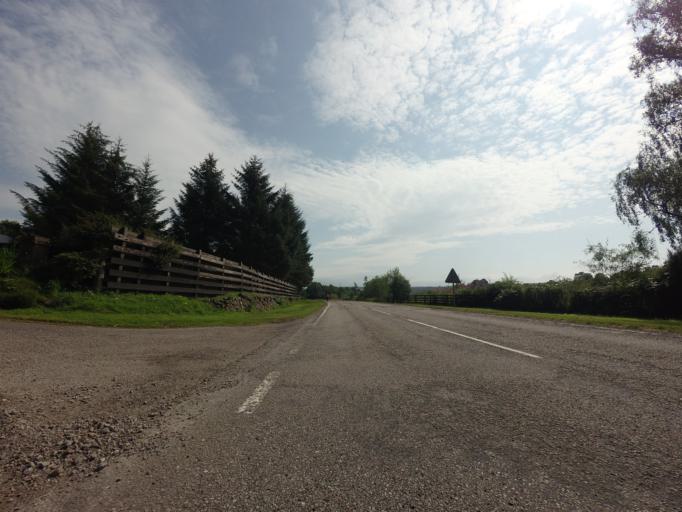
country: GB
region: Scotland
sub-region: Highland
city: Evanton
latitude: 57.9224
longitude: -4.3990
